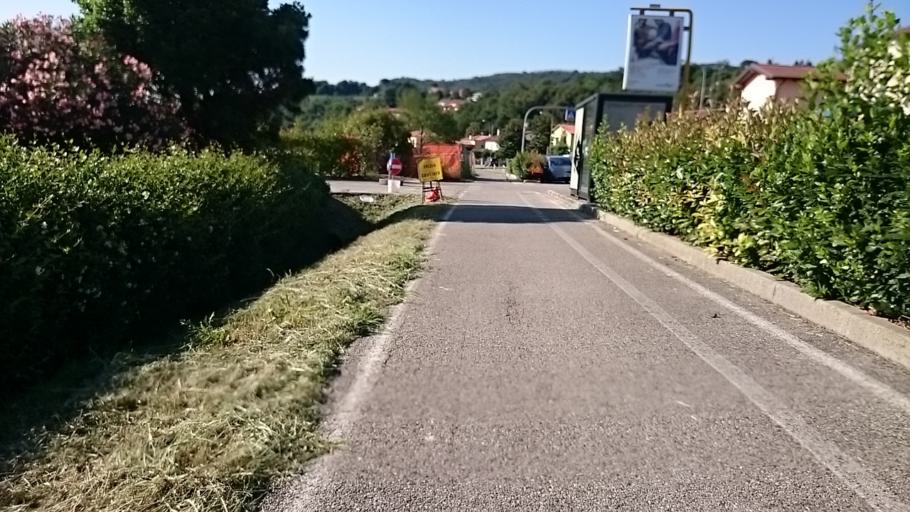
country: IT
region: Veneto
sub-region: Provincia di Vicenza
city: Longare
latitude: 45.4955
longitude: 11.5902
